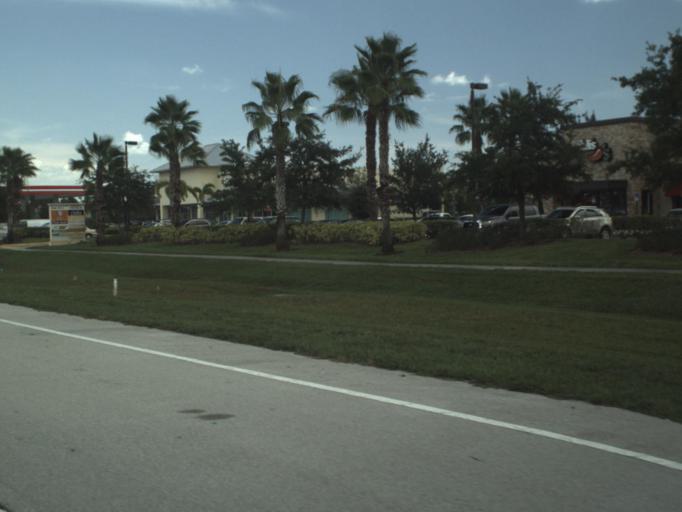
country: US
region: Florida
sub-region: Martin County
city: Port Salerno
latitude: 27.1532
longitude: -80.2190
